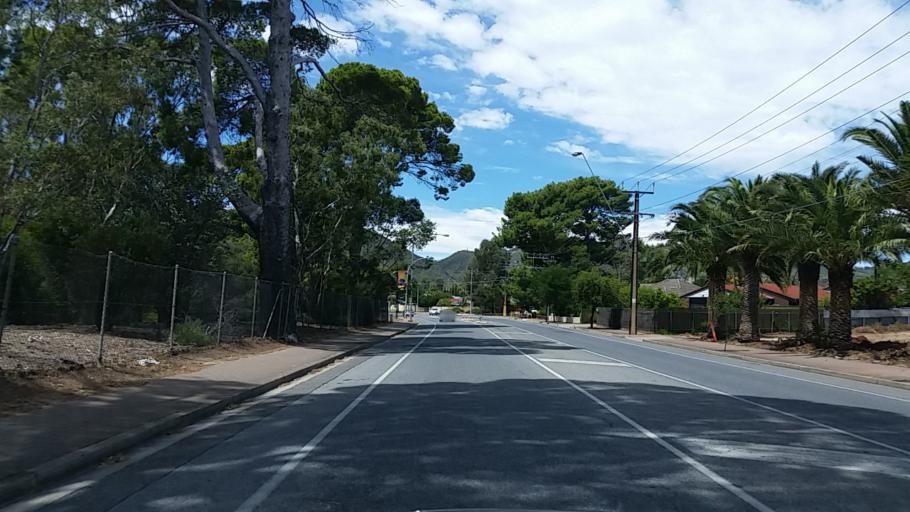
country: AU
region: South Australia
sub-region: Campbelltown
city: Athelstone
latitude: -34.8765
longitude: 138.6871
